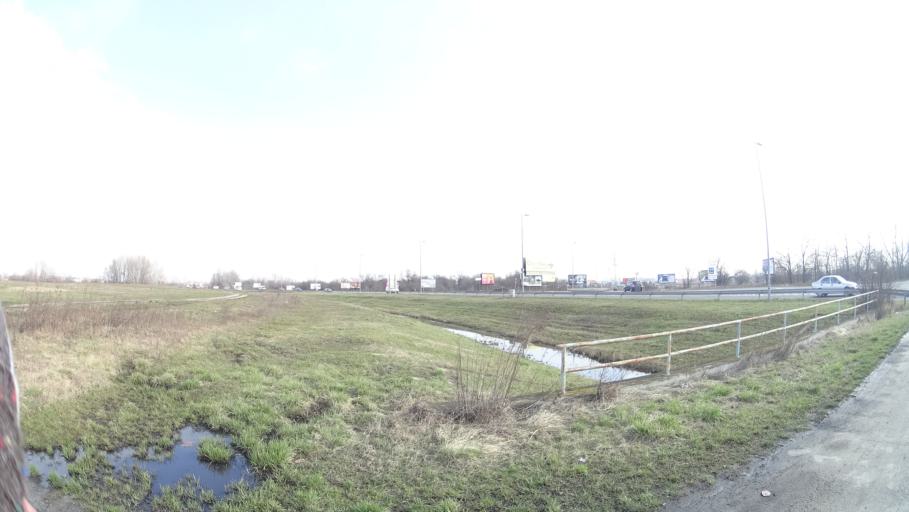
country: HU
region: Budapest
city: Budapest XIX. keruelet
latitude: 47.4192
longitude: 19.1475
